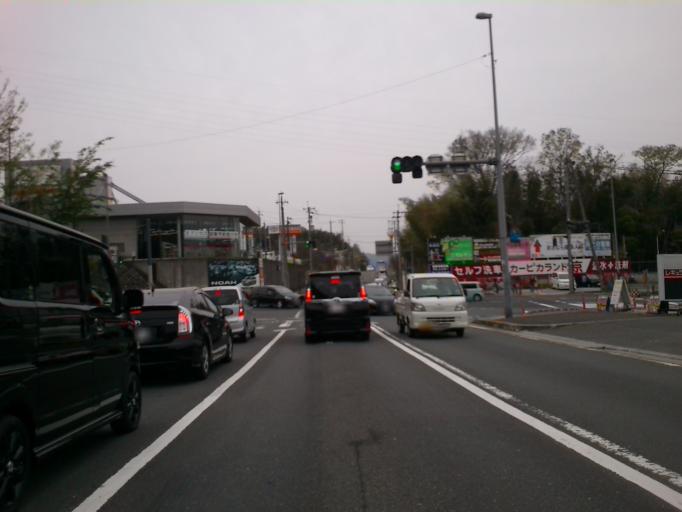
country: JP
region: Kyoto
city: Yawata
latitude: 34.8524
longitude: 135.7050
